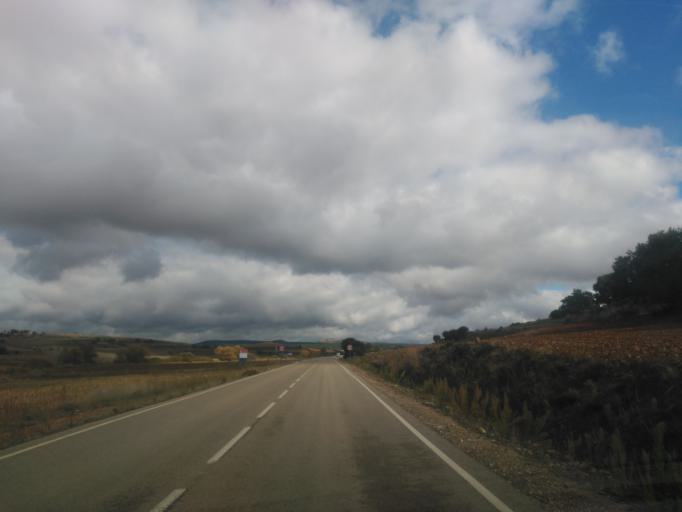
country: ES
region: Castille and Leon
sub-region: Provincia de Soria
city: Alcubilla de Avellaneda
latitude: 41.7483
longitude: -3.2828
